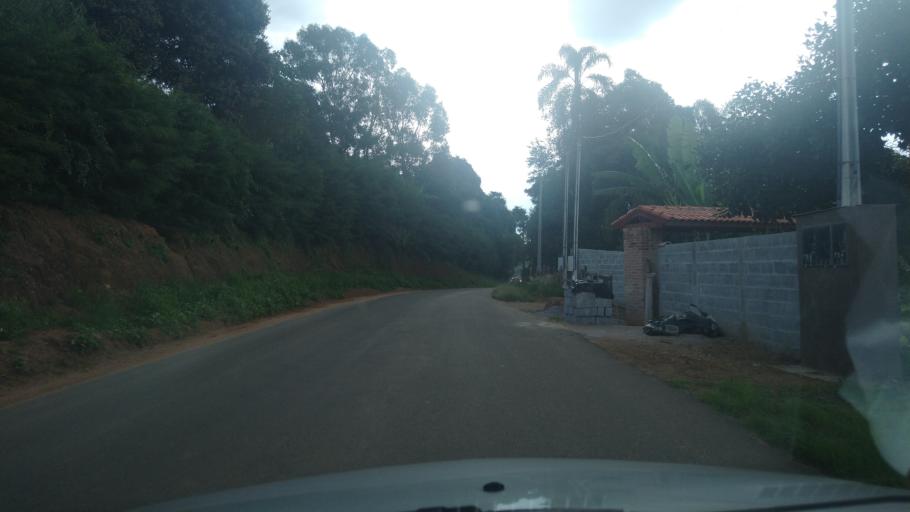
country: BR
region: Minas Gerais
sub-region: Extrema
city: Extrema
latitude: -22.7228
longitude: -46.3470
